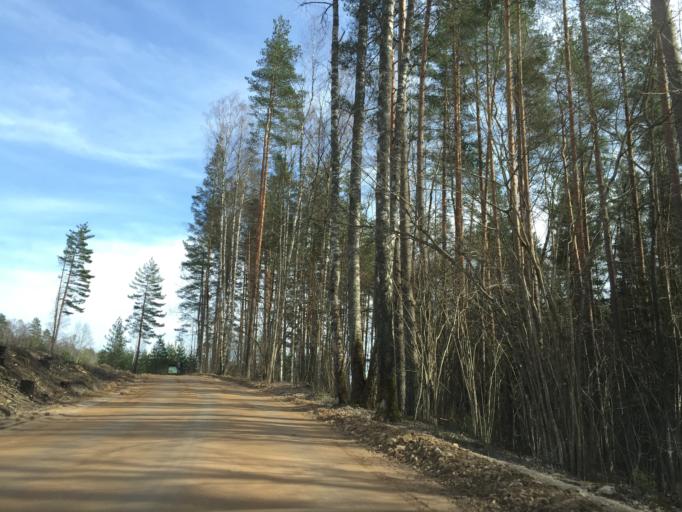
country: LV
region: Ikskile
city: Ikskile
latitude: 56.8432
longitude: 24.5419
